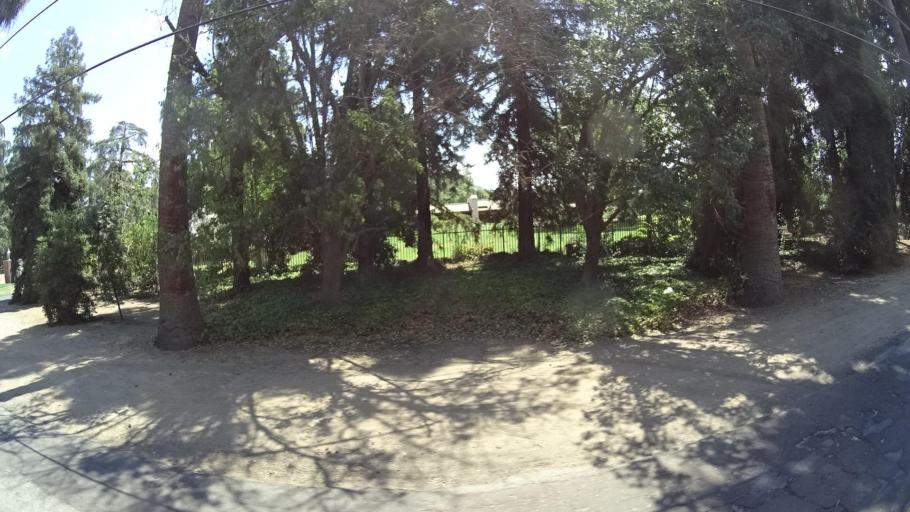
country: US
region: California
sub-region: Fresno County
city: Sunnyside
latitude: 36.7243
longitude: -119.7094
